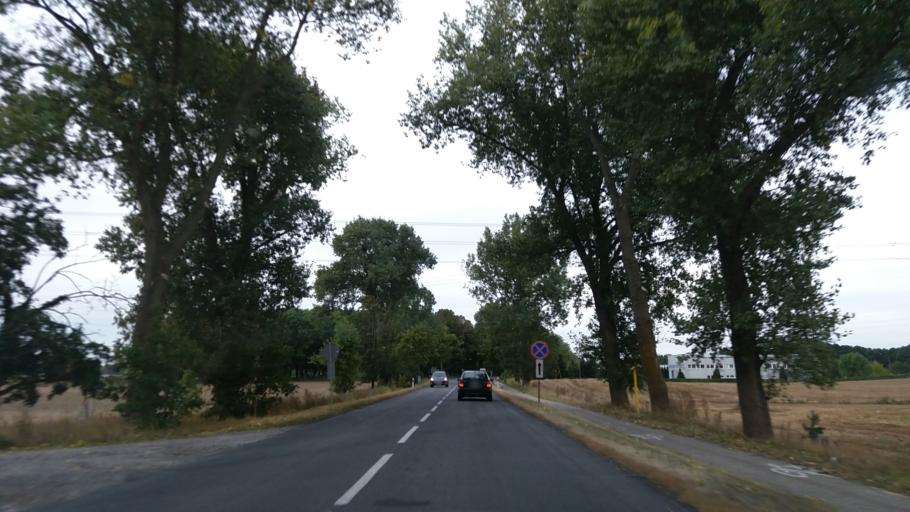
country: PL
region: Lubusz
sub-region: Powiat gorzowski
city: Klodawa
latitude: 52.7968
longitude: 15.2176
